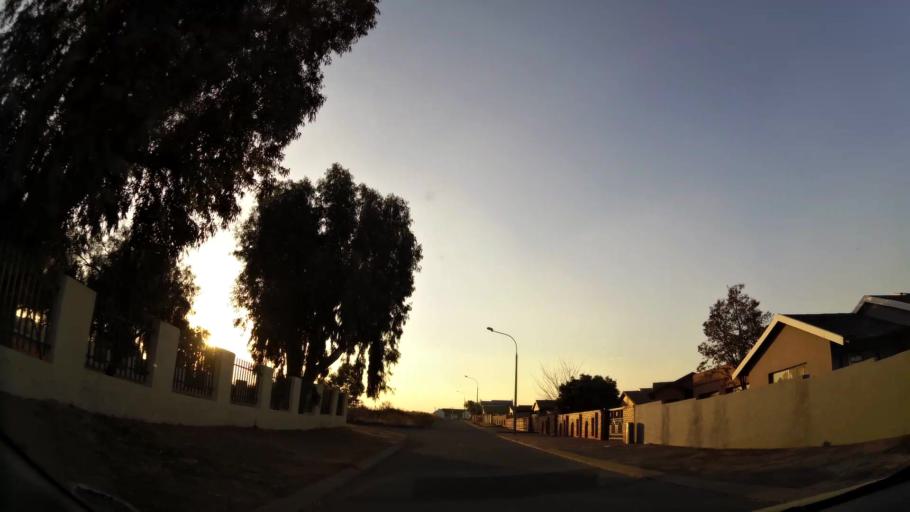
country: ZA
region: Gauteng
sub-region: West Rand District Municipality
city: Randfontein
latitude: -26.2085
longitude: 27.7051
